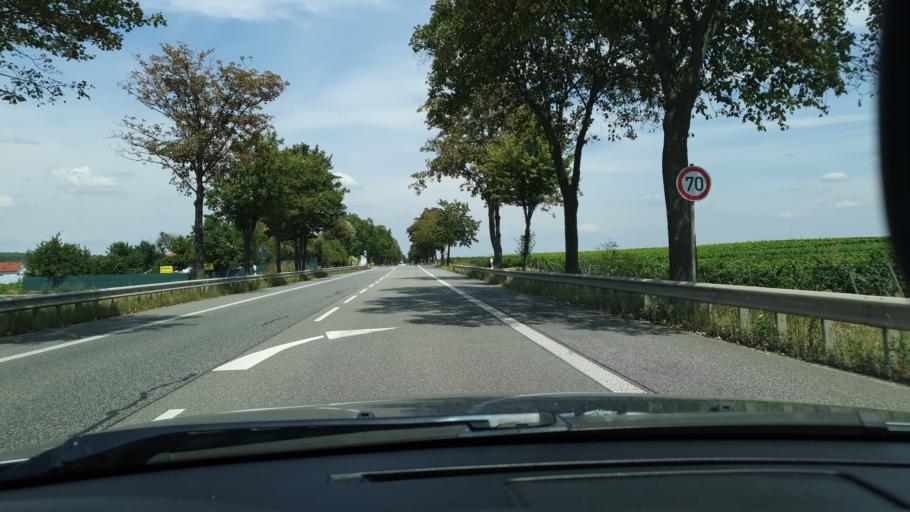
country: DE
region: Rheinland-Pfalz
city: Alsheim
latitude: 49.7646
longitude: 8.3524
